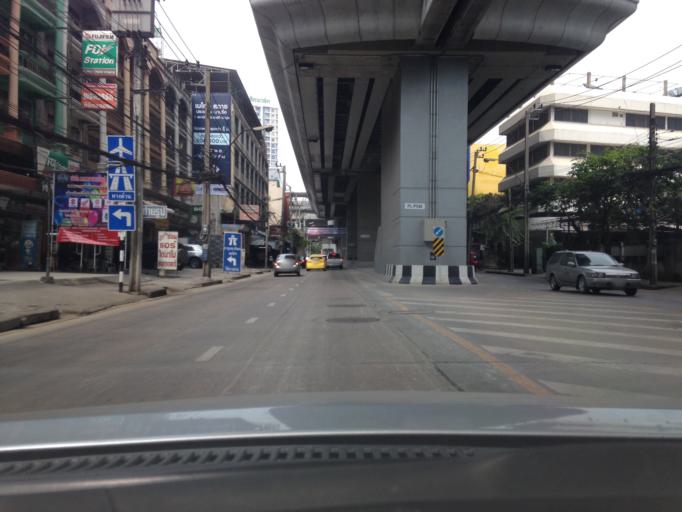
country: TH
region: Bangkok
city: Bang Sue
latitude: 13.8201
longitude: 100.5324
